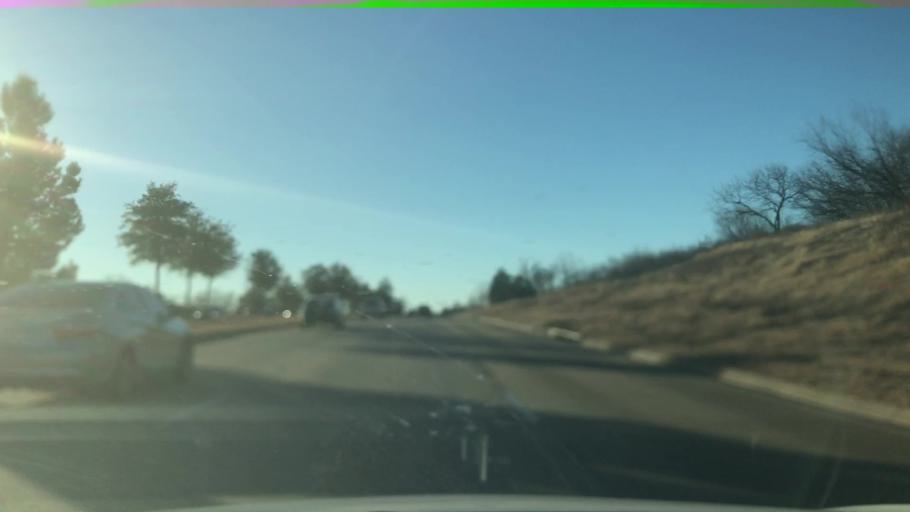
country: US
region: Texas
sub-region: Dallas County
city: Coppell
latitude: 32.9867
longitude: -97.0495
